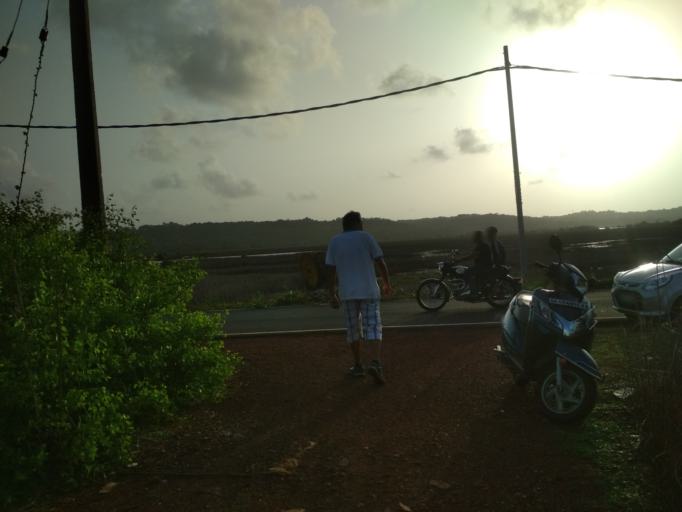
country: IN
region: Goa
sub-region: North Goa
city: Serula
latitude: 15.5290
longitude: 73.8579
